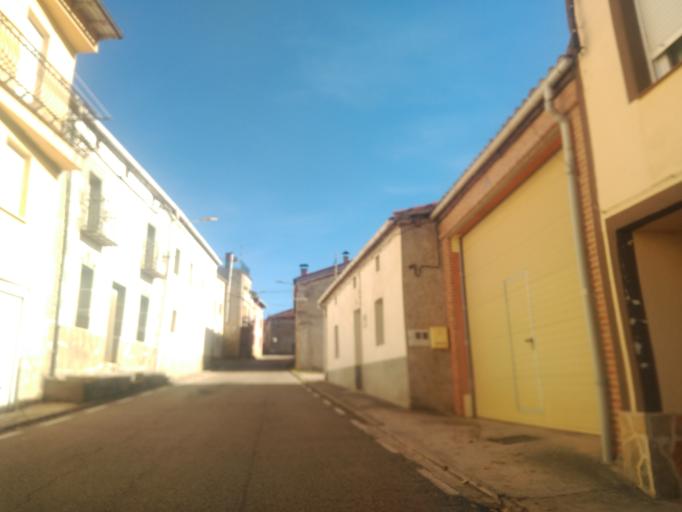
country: ES
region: Castille and Leon
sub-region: Provincia de Soria
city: Espejon
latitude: 41.8309
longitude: -3.2601
